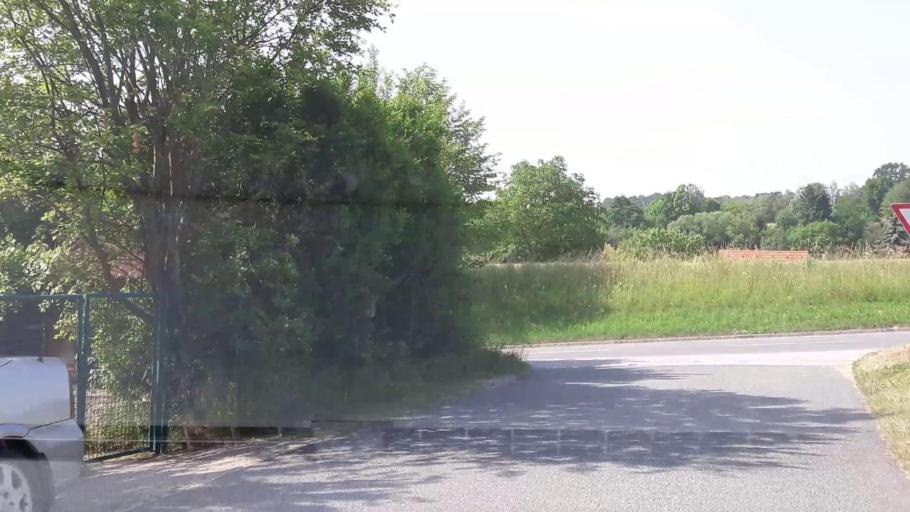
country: AT
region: Burgenland
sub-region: Politischer Bezirk Gussing
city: Stegersbach
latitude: 47.1604
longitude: 16.1580
